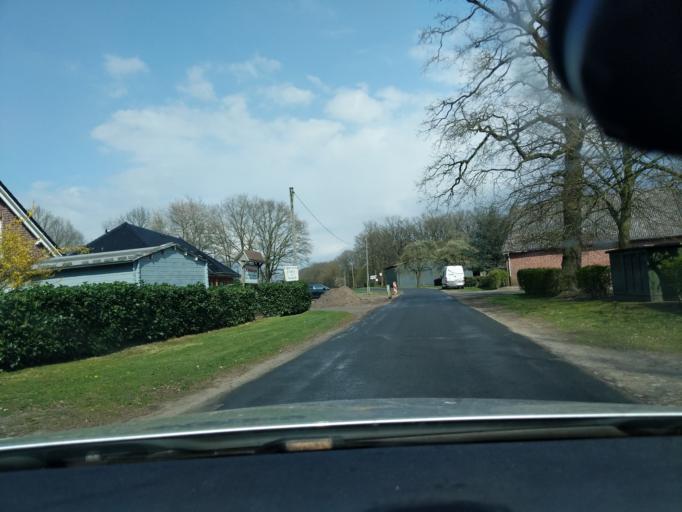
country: DE
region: Lower Saxony
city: Harsefeld
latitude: 53.4876
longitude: 9.5135
